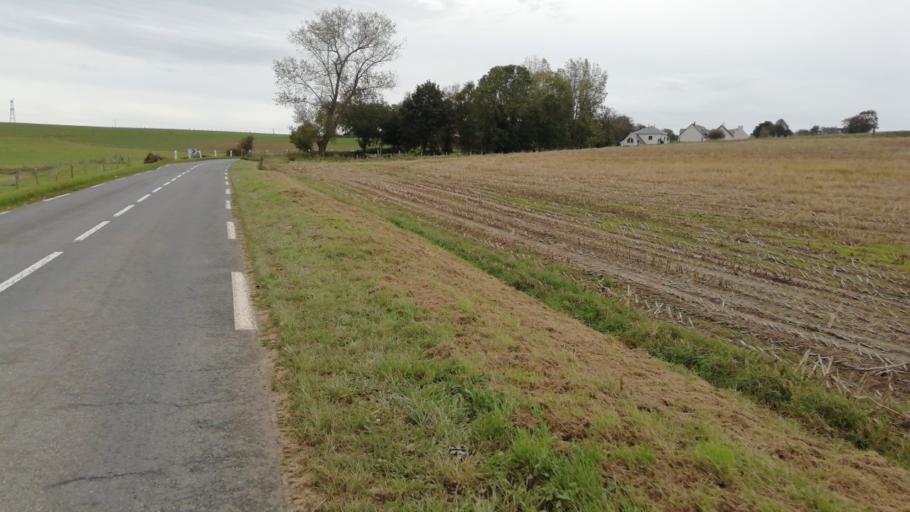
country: FR
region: Haute-Normandie
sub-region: Departement de la Seine-Maritime
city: Fontaine-la-Mallet
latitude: 49.5435
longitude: 0.1450
